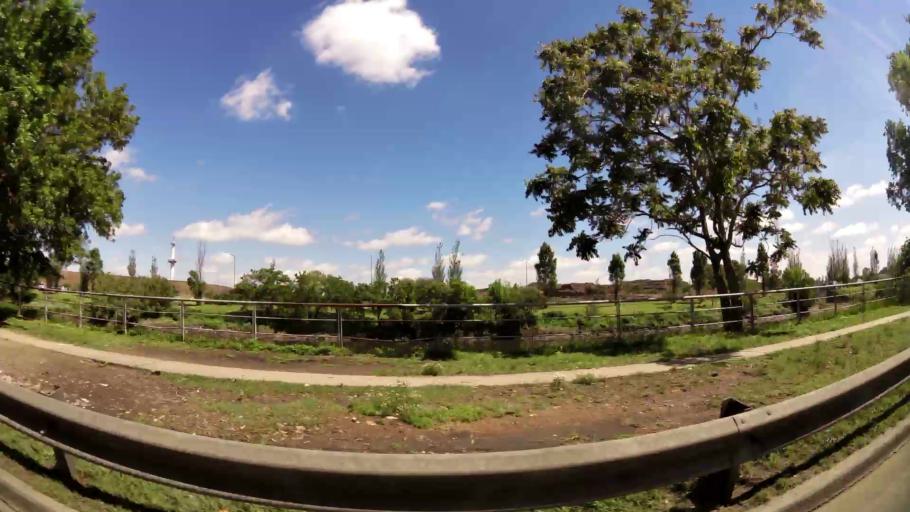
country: AR
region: Buenos Aires F.D.
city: Villa Lugano
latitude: -34.6738
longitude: -58.4338
